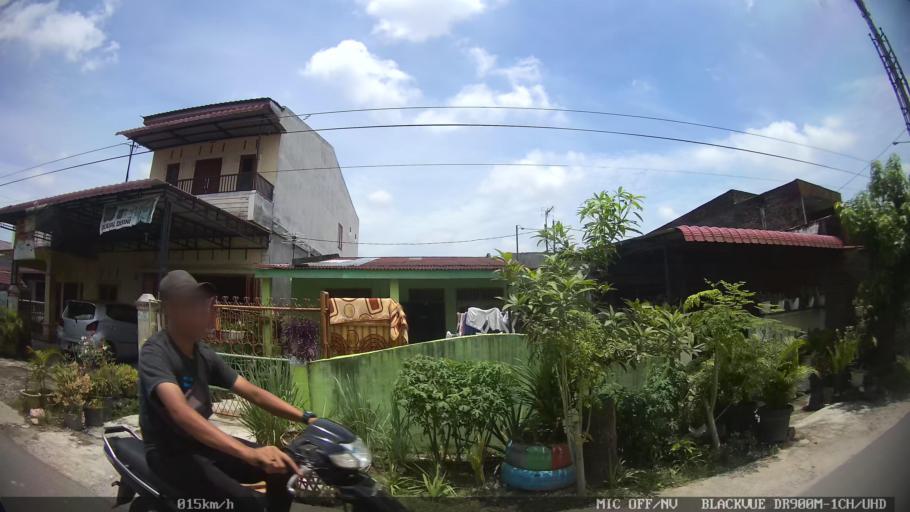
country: ID
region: North Sumatra
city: Perbaungan
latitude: 3.5428
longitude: 98.8778
